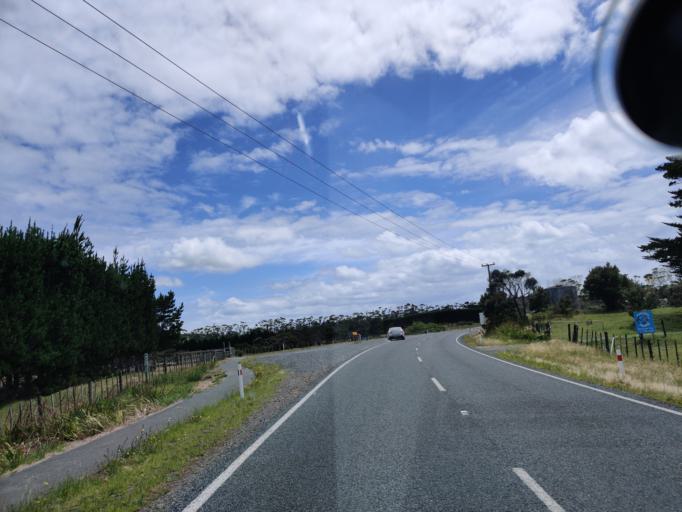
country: NZ
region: Northland
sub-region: Far North District
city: Kaitaia
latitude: -34.8291
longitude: 173.1280
